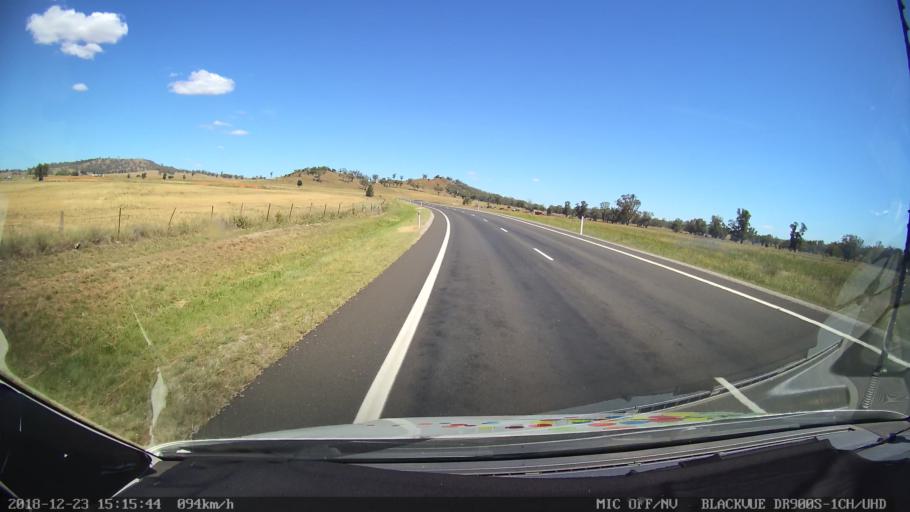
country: AU
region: New South Wales
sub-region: Tamworth Municipality
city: Manilla
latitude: -30.7901
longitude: 150.7443
